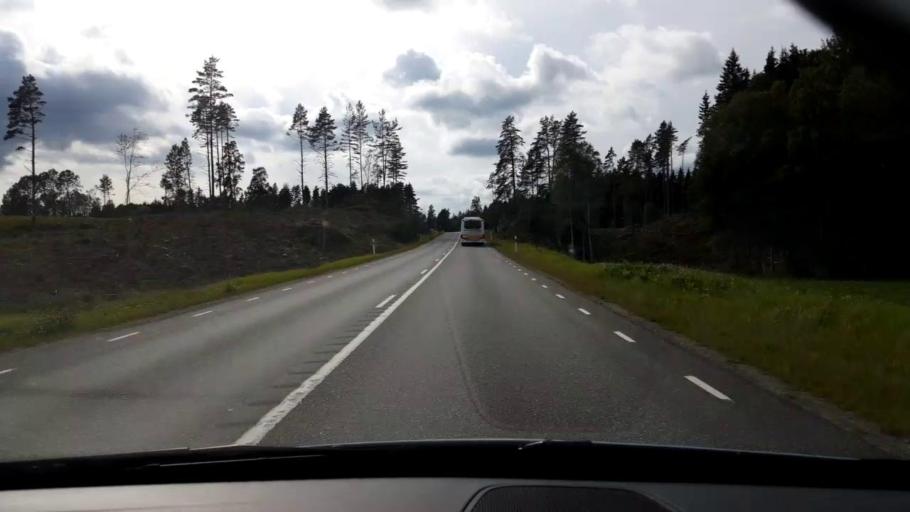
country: SE
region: Joenkoeping
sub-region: Vetlanda Kommun
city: Landsbro
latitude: 57.3966
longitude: 14.8622
